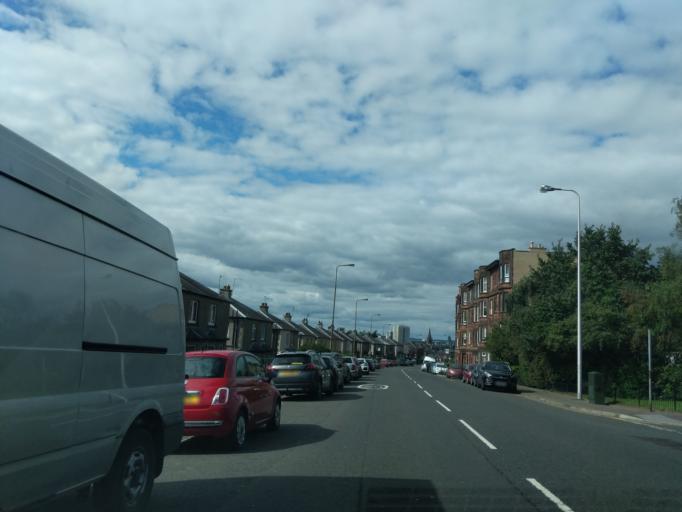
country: GB
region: Scotland
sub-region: West Lothian
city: Seafield
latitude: 55.9642
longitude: -3.1619
